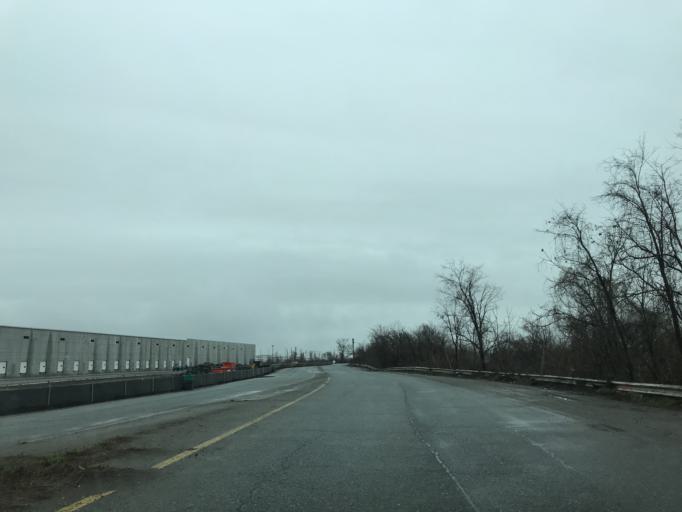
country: US
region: Maryland
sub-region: Baltimore County
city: Dundalk
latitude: 39.2344
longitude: -76.4930
